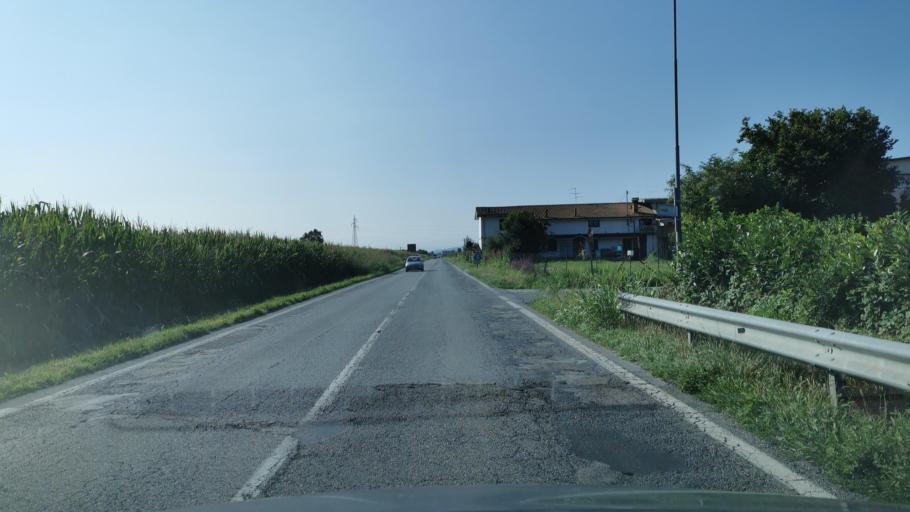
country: IT
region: Piedmont
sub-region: Provincia di Torino
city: Cavour
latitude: 44.7597
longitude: 7.3997
